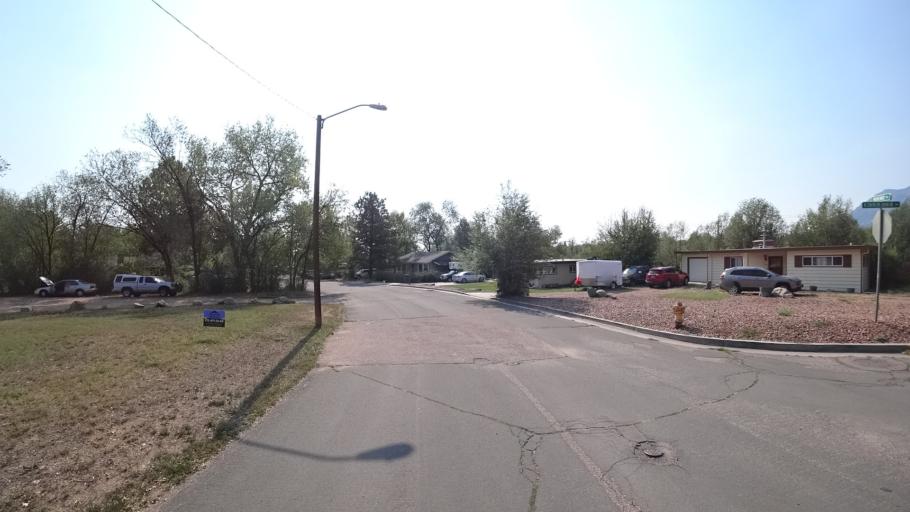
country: US
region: Colorado
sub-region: El Paso County
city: Colorado Springs
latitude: 38.8107
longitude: -104.8366
